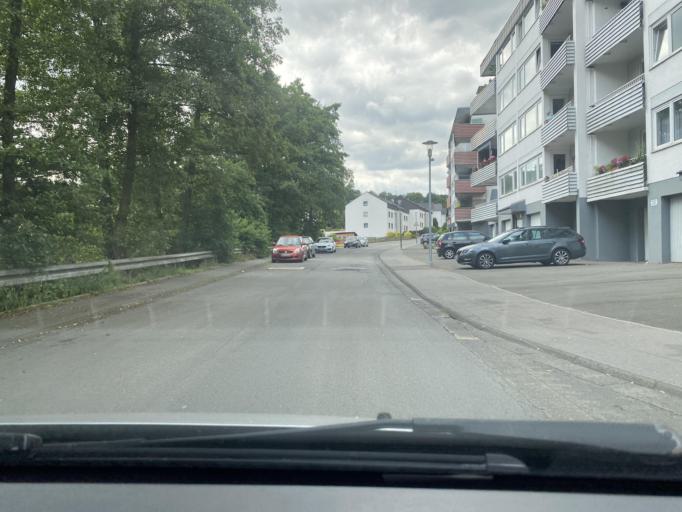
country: DE
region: North Rhine-Westphalia
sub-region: Regierungsbezirk Arnsberg
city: Luedenscheid
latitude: 51.2576
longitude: 7.6221
